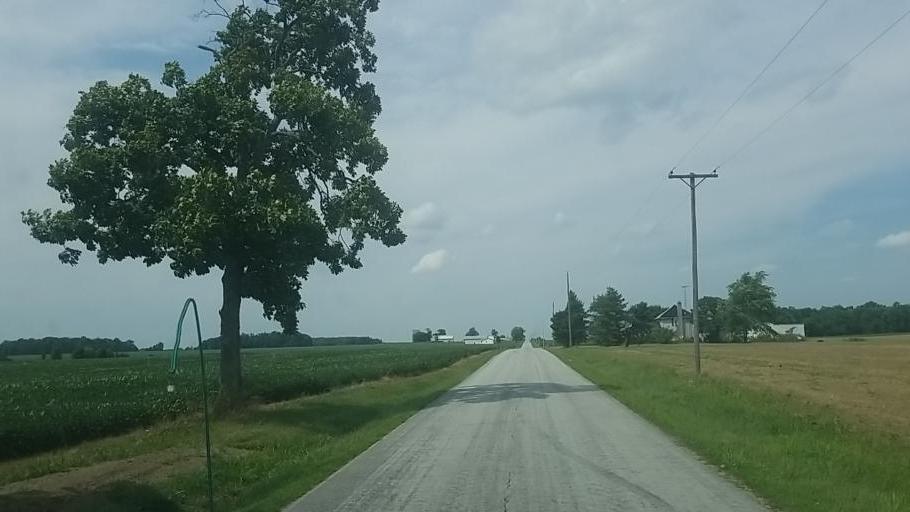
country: US
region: Ohio
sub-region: Hardin County
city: Forest
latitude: 40.7603
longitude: -83.5572
